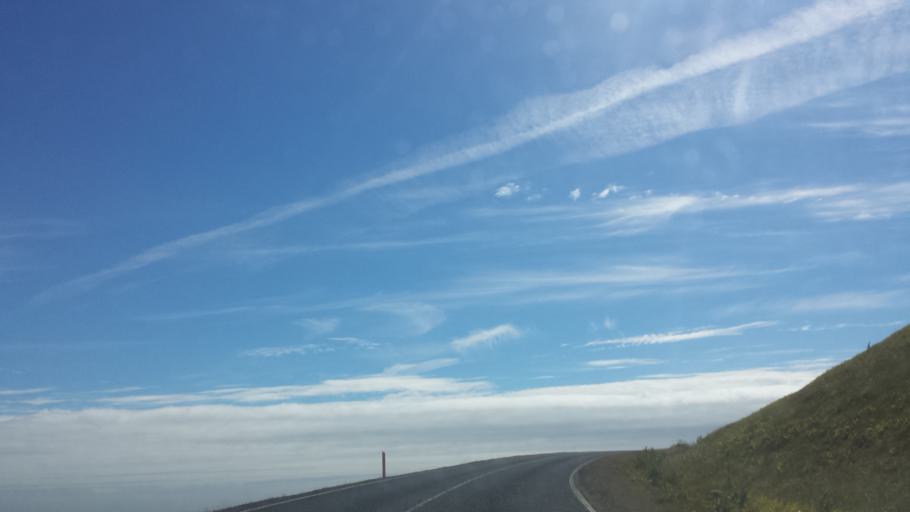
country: IS
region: South
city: Vestmannaeyjar
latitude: 63.4299
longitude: -20.2554
